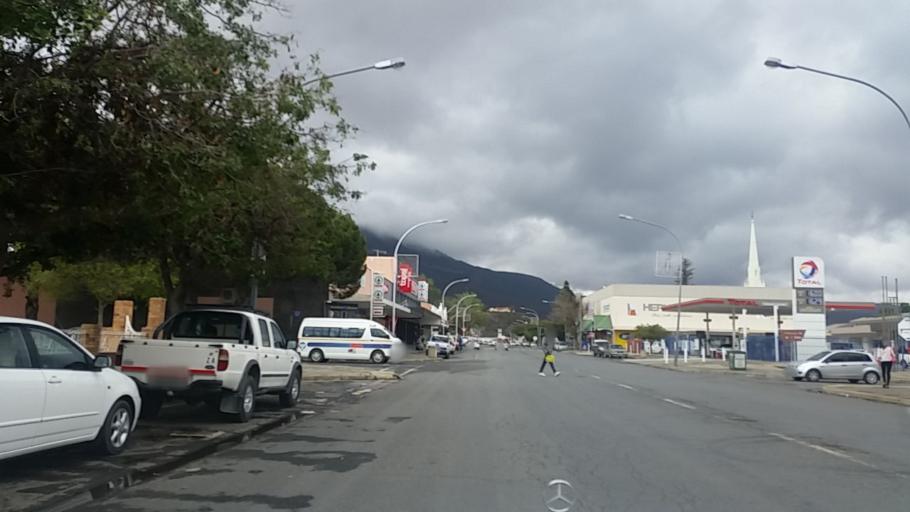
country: ZA
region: Eastern Cape
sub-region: Cacadu District Municipality
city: Graaff-Reinet
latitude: -32.2497
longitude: 24.5325
